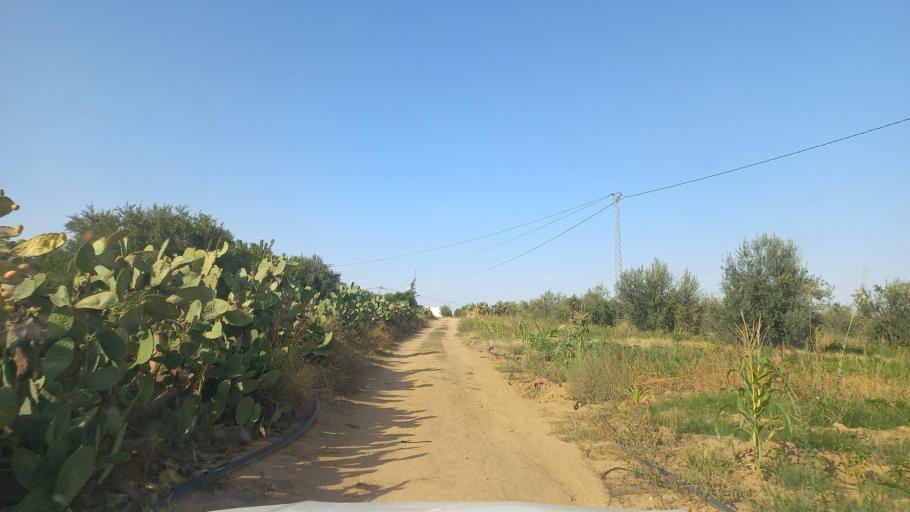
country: TN
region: Al Qasrayn
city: Kasserine
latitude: 35.2567
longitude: 9.0249
